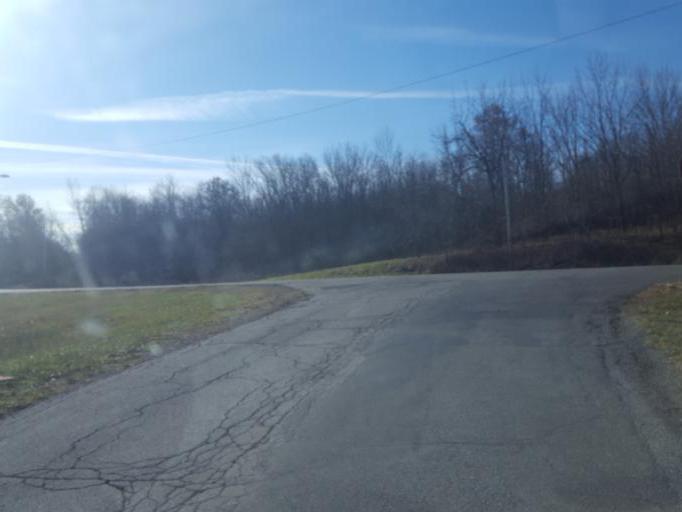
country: US
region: Ohio
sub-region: Richland County
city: Ontario
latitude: 40.8011
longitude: -82.5710
